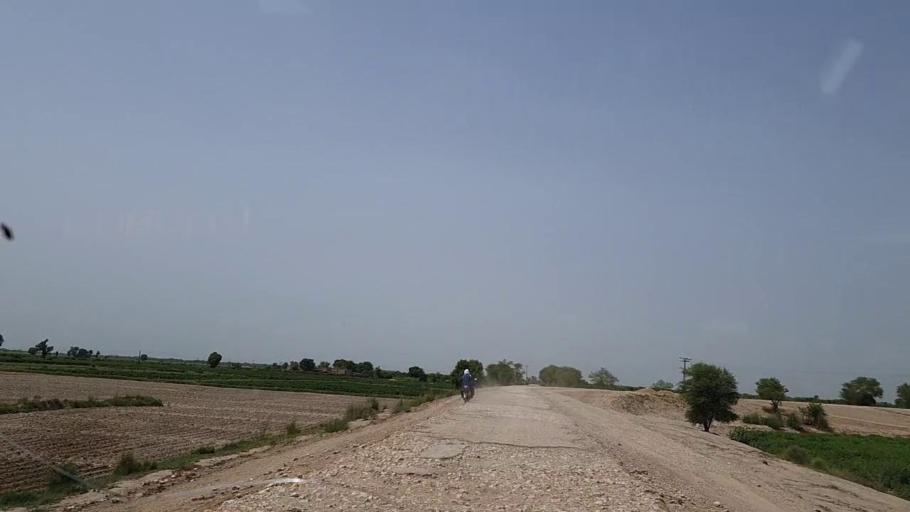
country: PK
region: Sindh
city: Tharu Shah
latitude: 27.0380
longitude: 68.1103
